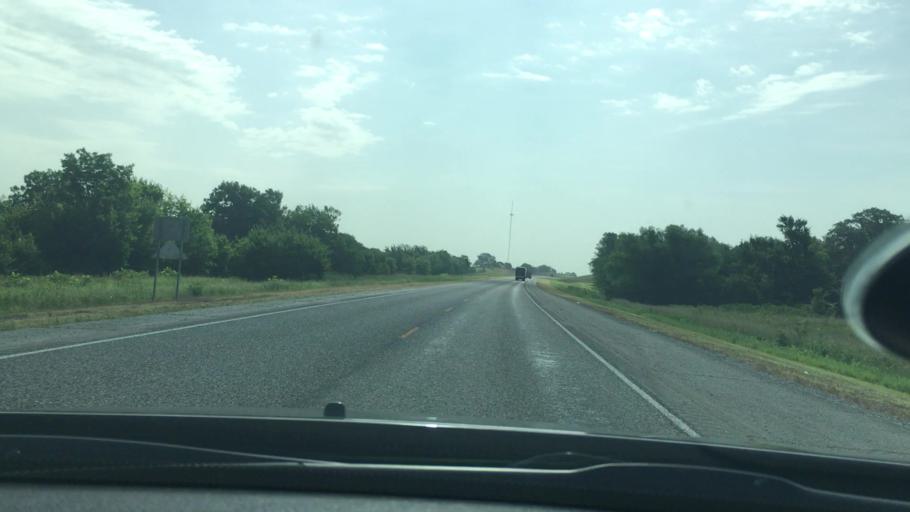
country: US
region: Oklahoma
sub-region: Coal County
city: Coalgate
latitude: 34.5999
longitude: -96.3248
